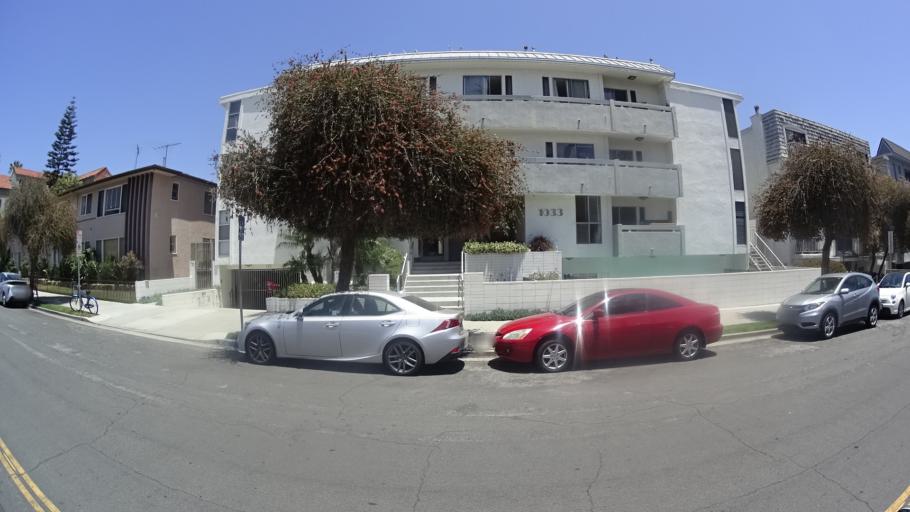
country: US
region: California
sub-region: Los Angeles County
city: Santa Monica
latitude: 34.0204
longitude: -118.5018
